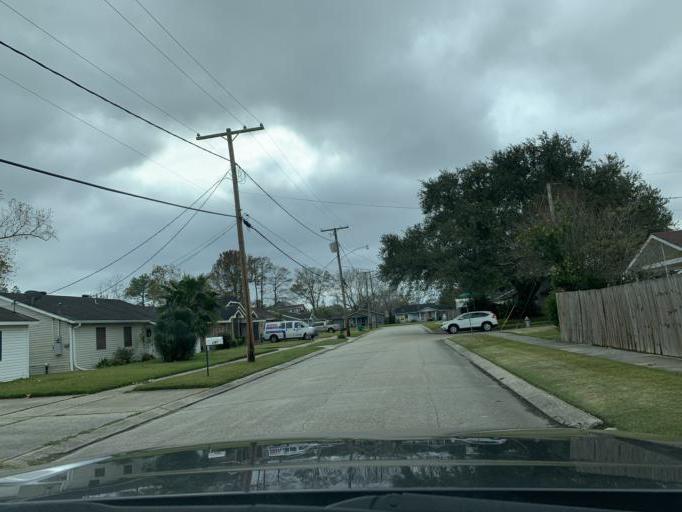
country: US
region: Louisiana
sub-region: Jefferson Parish
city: River Ridge
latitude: 29.9539
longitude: -90.2391
